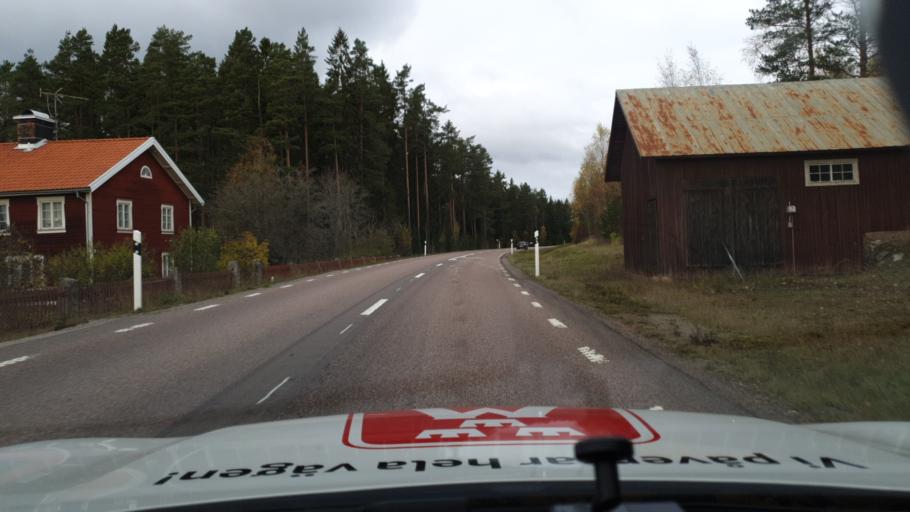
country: SE
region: Gaevleborg
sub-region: Gavle Kommun
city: Hedesunda
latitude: 60.4303
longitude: 16.9698
